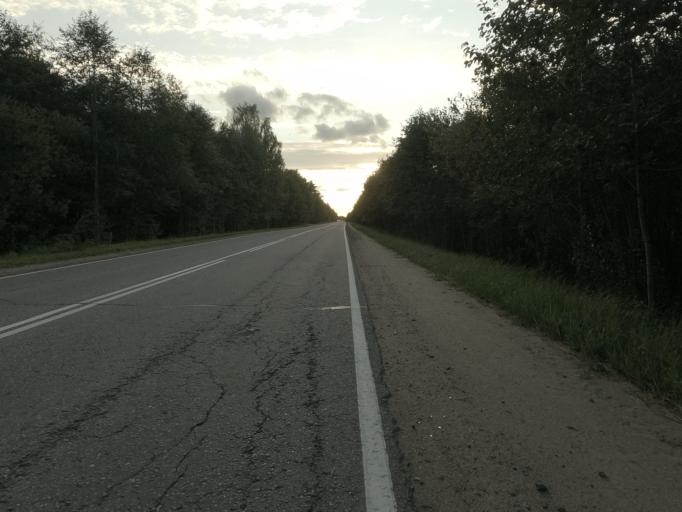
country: RU
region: Leningrad
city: Mga
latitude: 59.7605
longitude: 31.0121
